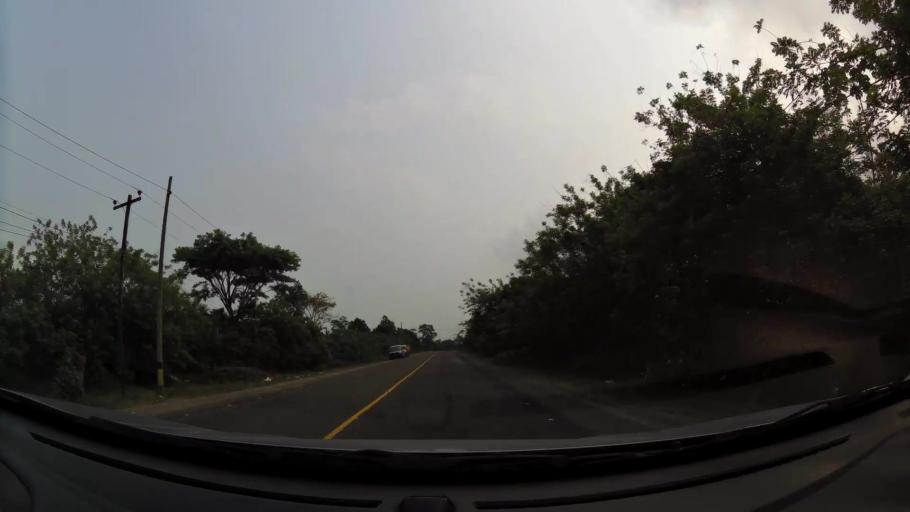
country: HN
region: Atlantida
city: Mezapa
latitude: 15.5689
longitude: -87.6186
